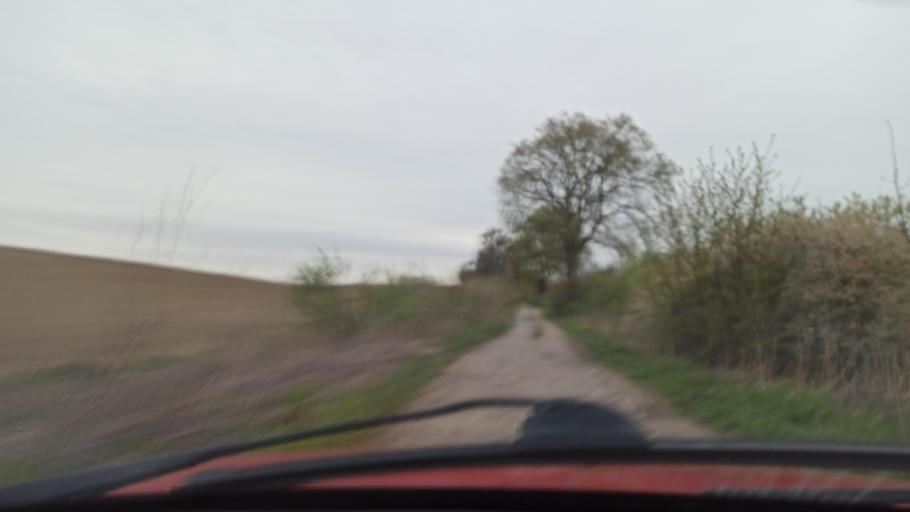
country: PL
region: Kujawsko-Pomorskie
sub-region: Powiat grudziadzki
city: Lasin
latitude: 53.5772
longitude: 19.0896
